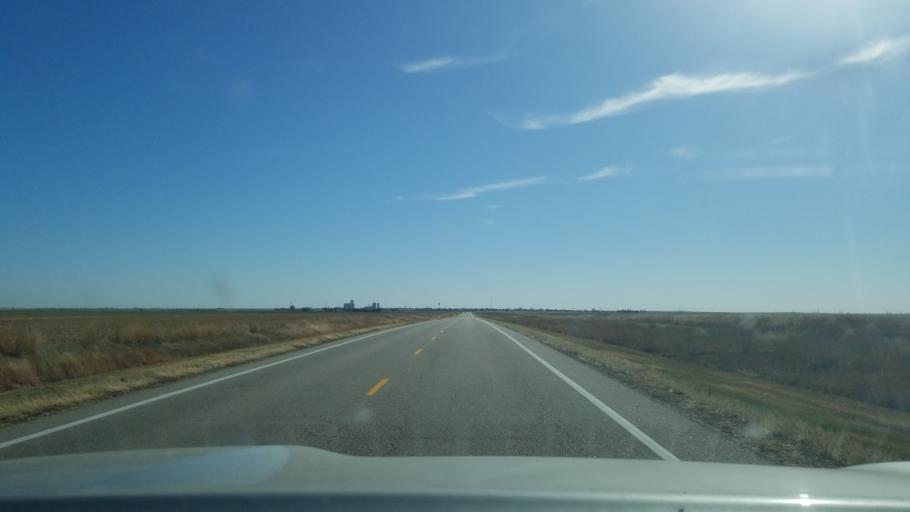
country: US
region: Kansas
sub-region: Kiowa County
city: Greensburg
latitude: 37.5708
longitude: -99.6634
